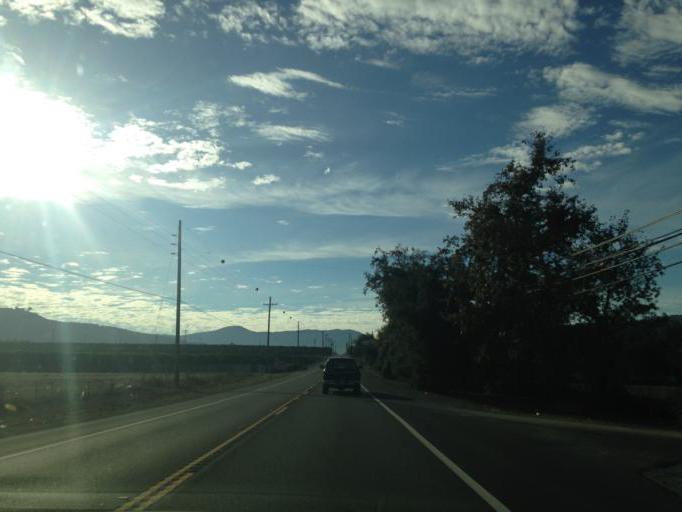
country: US
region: California
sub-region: San Diego County
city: Valley Center
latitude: 33.3232
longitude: -116.9961
